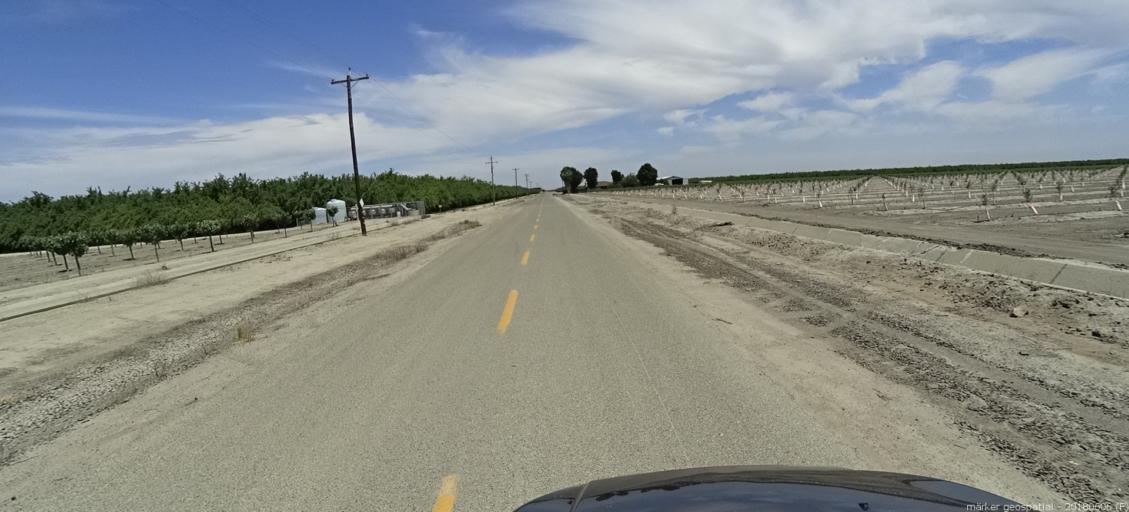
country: US
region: California
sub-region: Fresno County
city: Firebaugh
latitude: 36.8388
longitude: -120.3912
